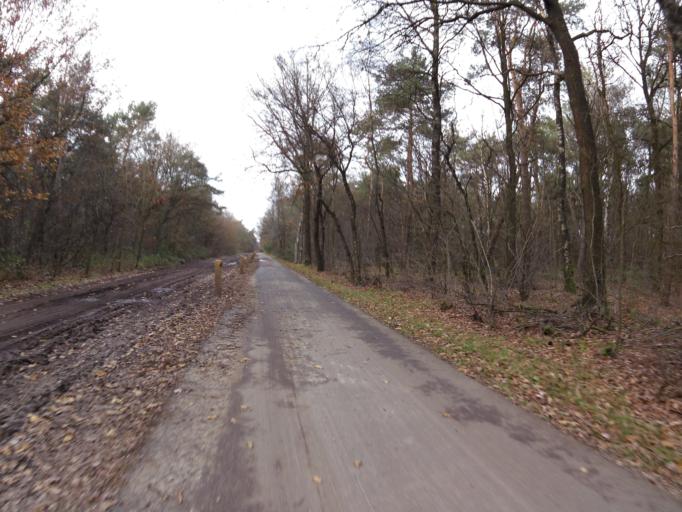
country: NL
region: North Brabant
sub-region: Gemeente Uden
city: Uden
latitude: 51.7025
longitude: 5.5965
